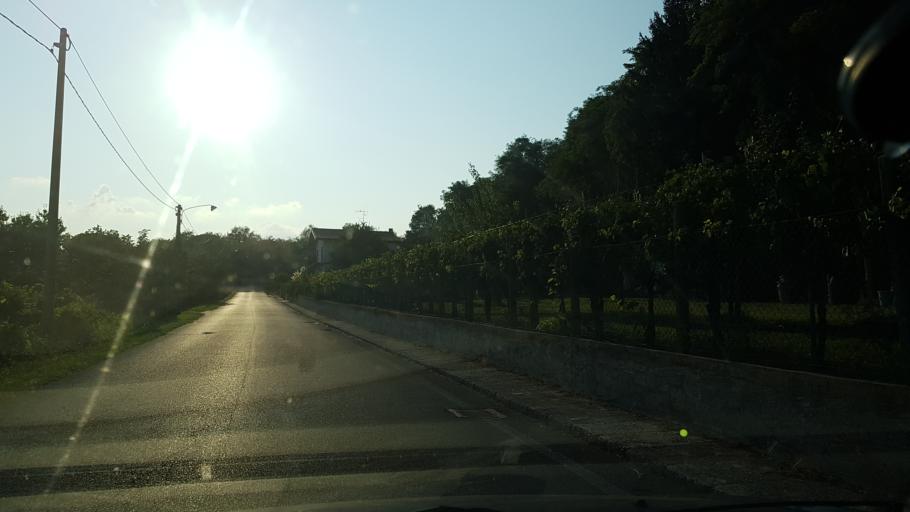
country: IT
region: Friuli Venezia Giulia
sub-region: Provincia di Gorizia
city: Savogna d'Isonzo
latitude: 45.9378
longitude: 13.5870
